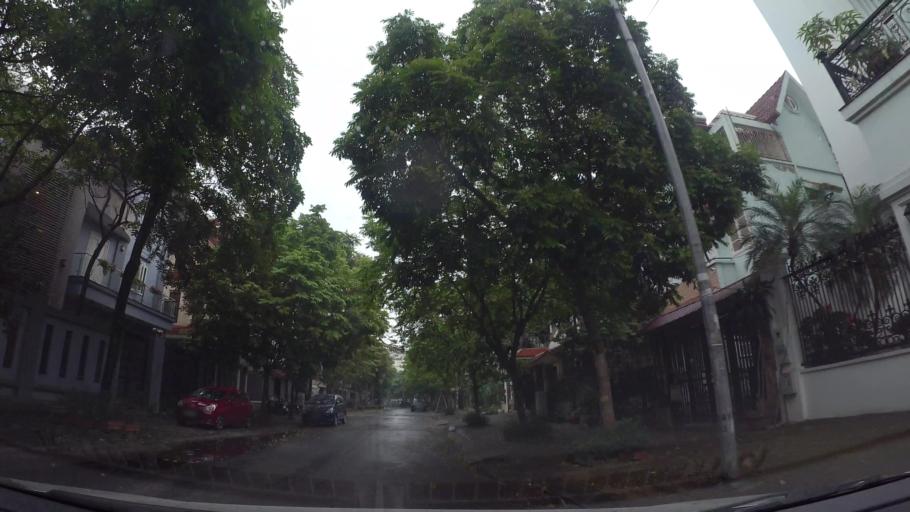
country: VN
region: Ha Noi
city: Cau Giay
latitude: 21.0196
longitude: 105.7964
